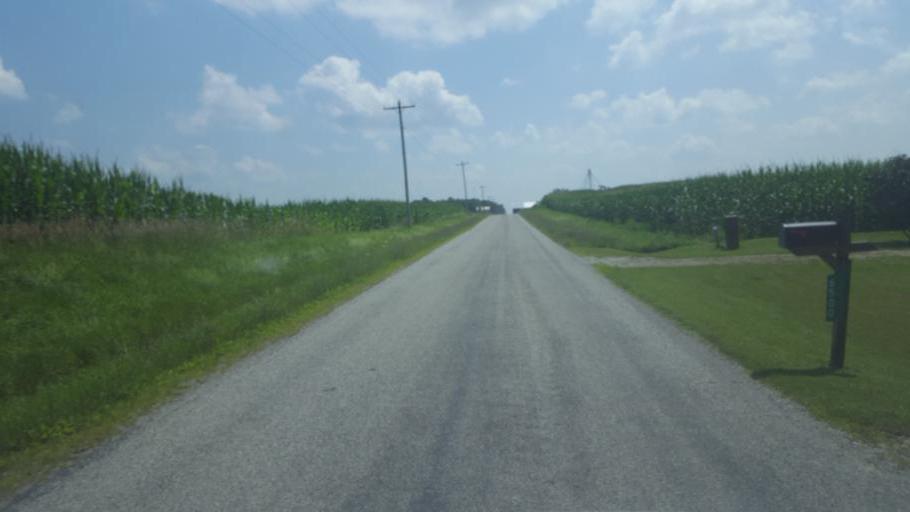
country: US
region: Ohio
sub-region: Richland County
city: Lexington
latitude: 40.6285
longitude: -82.6902
